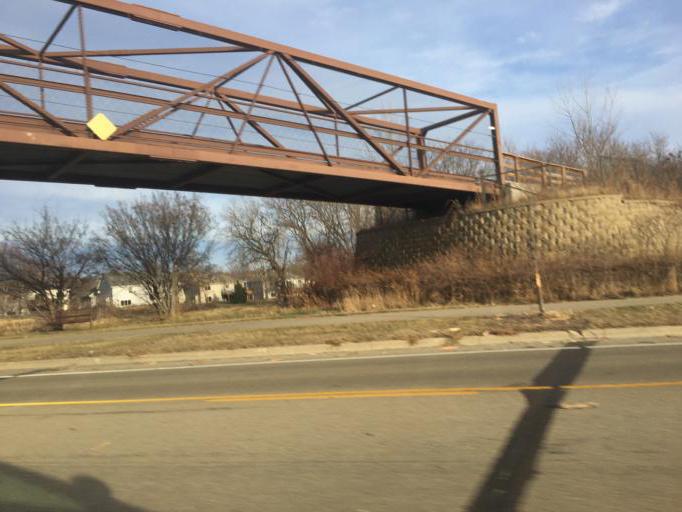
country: US
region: Minnesota
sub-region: Olmsted County
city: Oronoco
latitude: 44.0818
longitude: -92.5388
